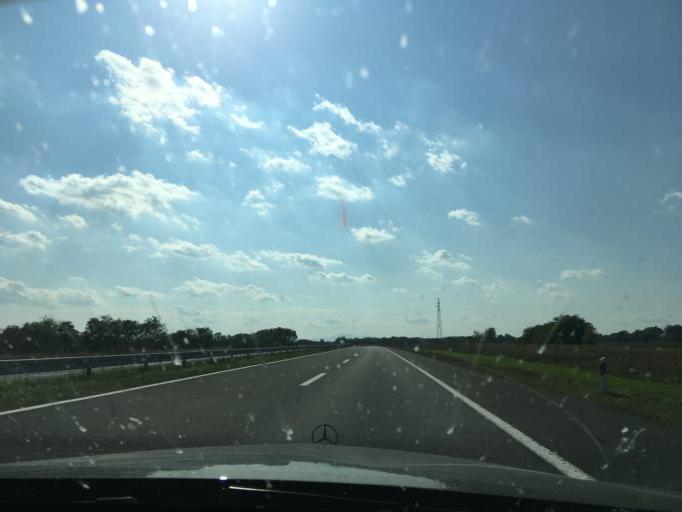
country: HR
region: Medimurska
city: Domasinec
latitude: 46.4063
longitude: 16.5848
